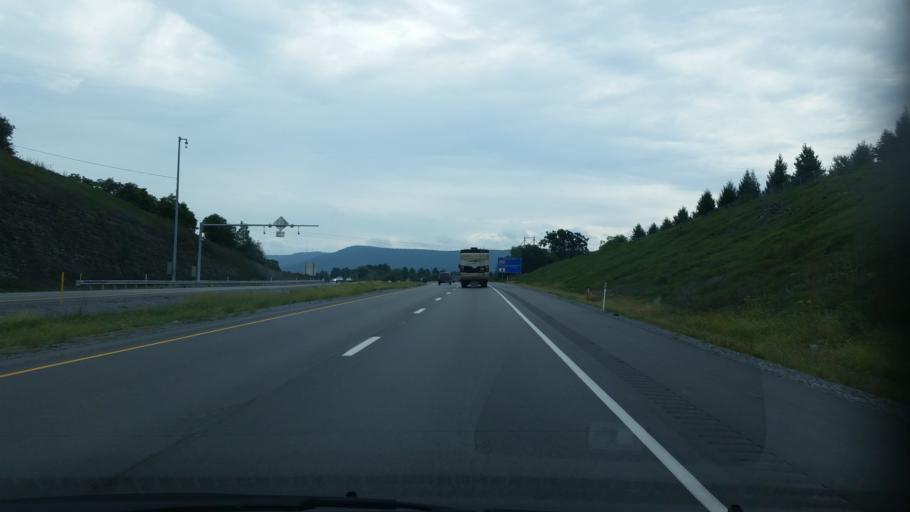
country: US
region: Pennsylvania
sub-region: Centre County
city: Lemont
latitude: 40.7968
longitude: -77.8222
